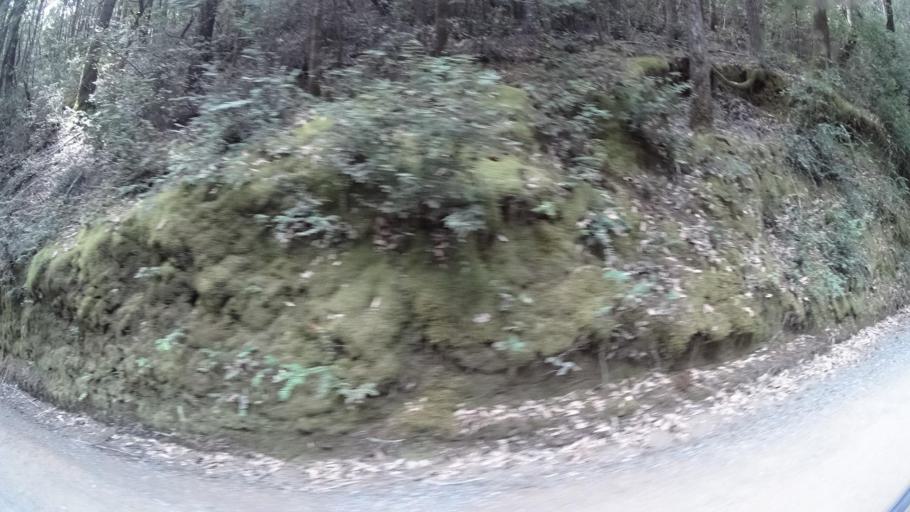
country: US
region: California
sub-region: Humboldt County
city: Redway
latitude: 40.0427
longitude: -123.8453
